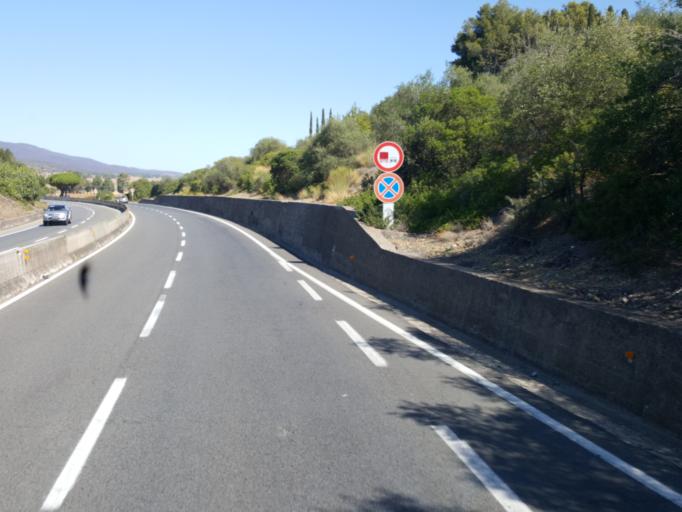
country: IT
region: Tuscany
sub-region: Provincia di Grosseto
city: Fonteblanda
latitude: 42.5667
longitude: 11.1725
